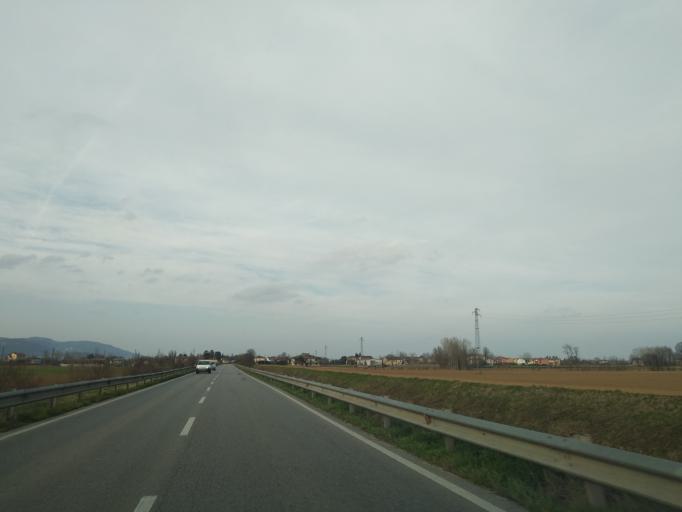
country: IT
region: Veneto
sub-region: Provincia di Vicenza
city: Ponte di Barbarano
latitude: 45.4036
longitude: 11.5814
